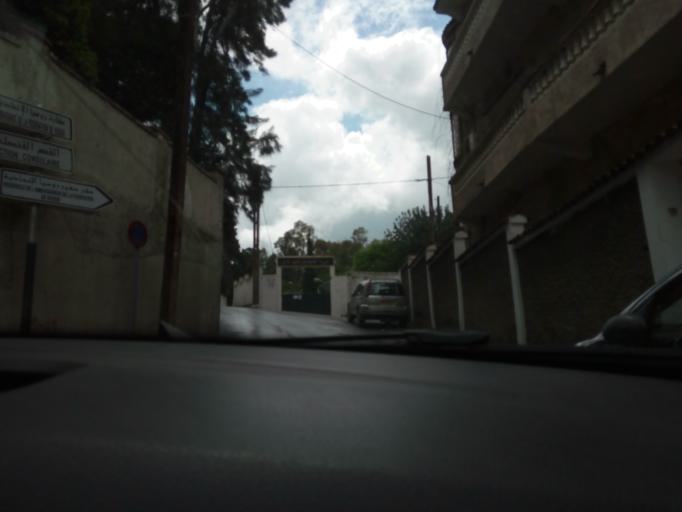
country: DZ
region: Alger
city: Algiers
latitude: 36.7653
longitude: 3.0354
